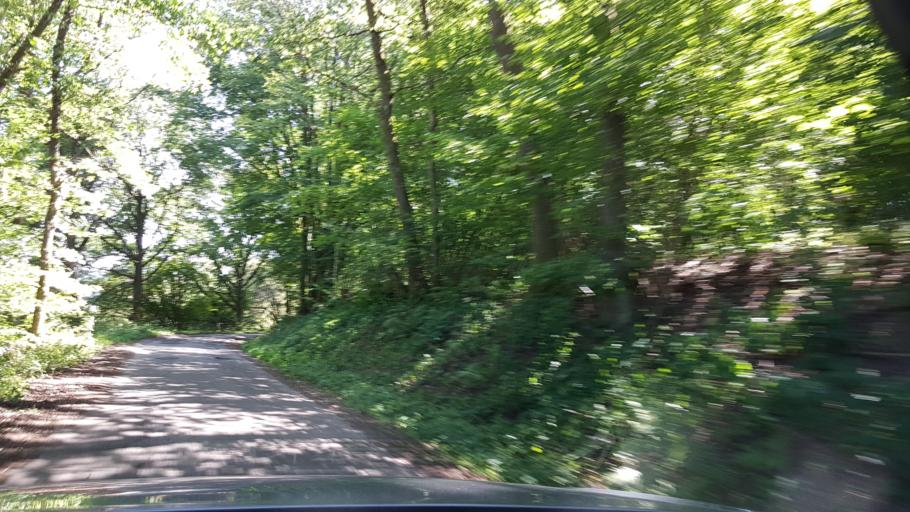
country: DE
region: Rheinland-Pfalz
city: Breitenbach
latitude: 49.4799
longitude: 7.2519
